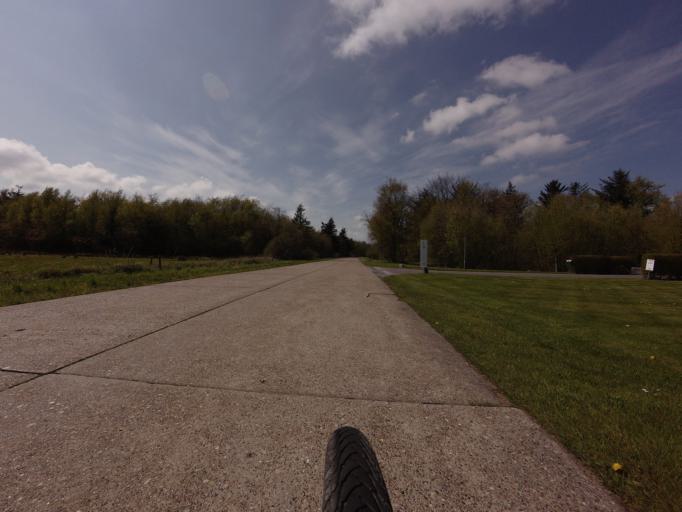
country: DK
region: North Denmark
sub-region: Jammerbugt Kommune
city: Brovst
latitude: 57.1644
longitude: 9.4873
